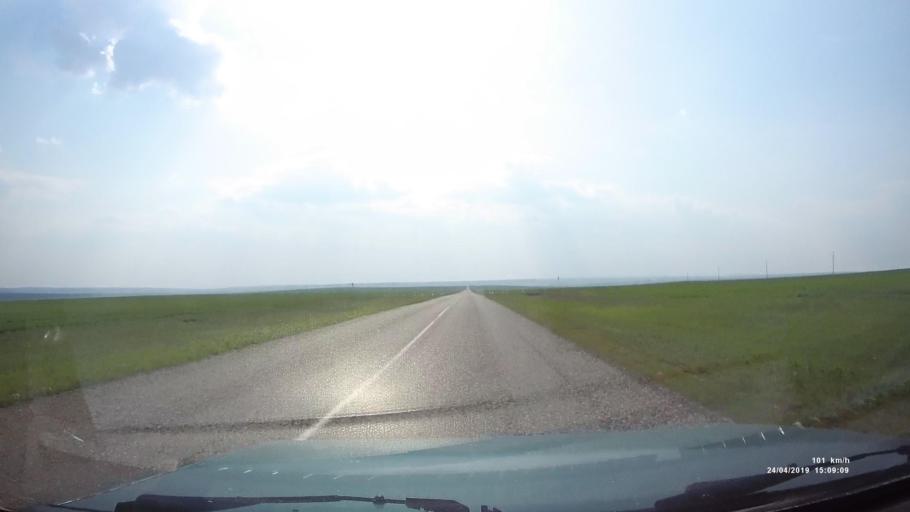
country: RU
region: Rostov
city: Remontnoye
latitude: 46.5567
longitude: 43.3678
